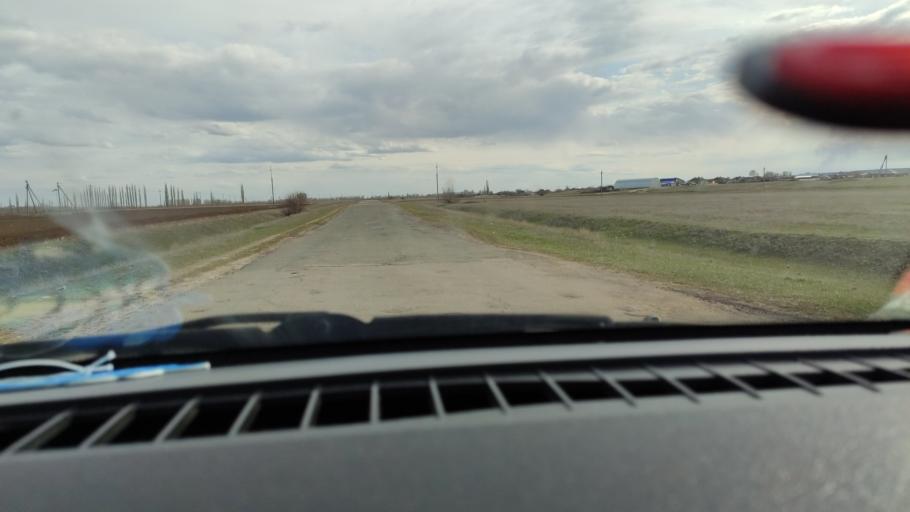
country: RU
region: Saratov
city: Rovnoye
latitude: 50.9340
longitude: 46.0942
